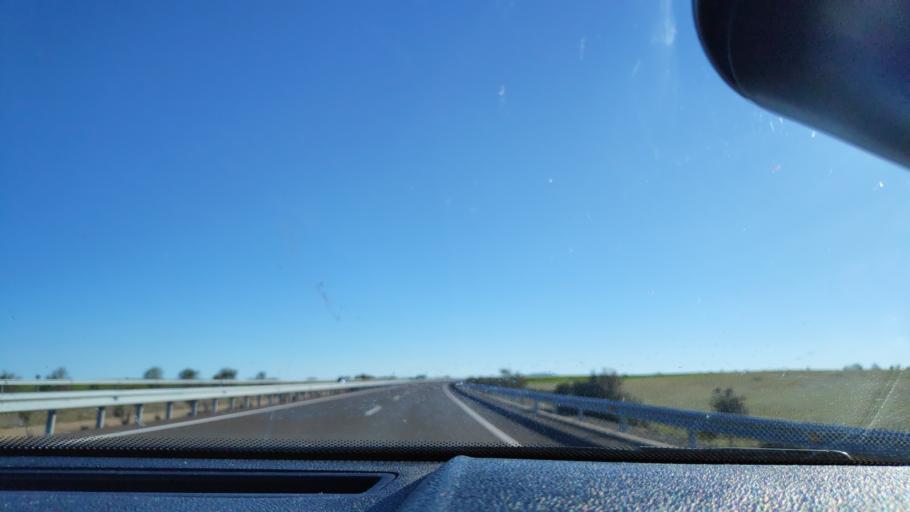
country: ES
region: Extremadura
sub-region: Provincia de Badajoz
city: Fuente de Cantos
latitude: 38.2109
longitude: -6.2873
